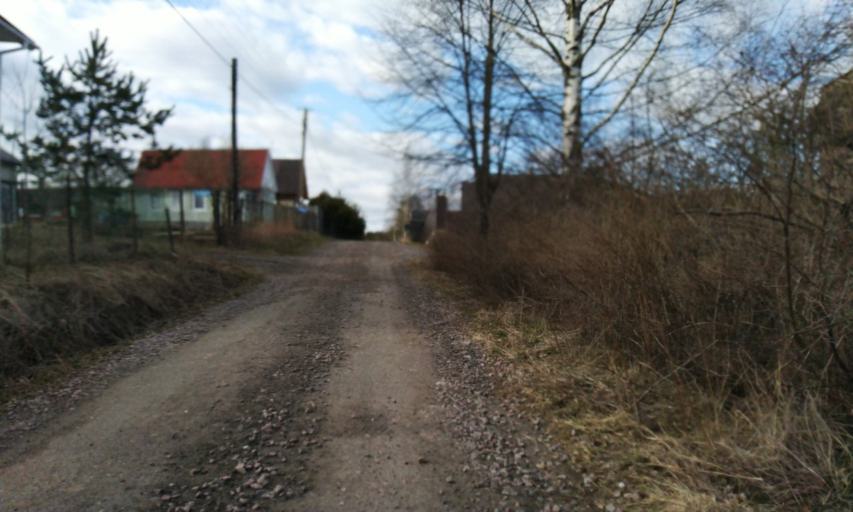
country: RU
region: Leningrad
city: Toksovo
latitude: 60.1291
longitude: 30.4891
